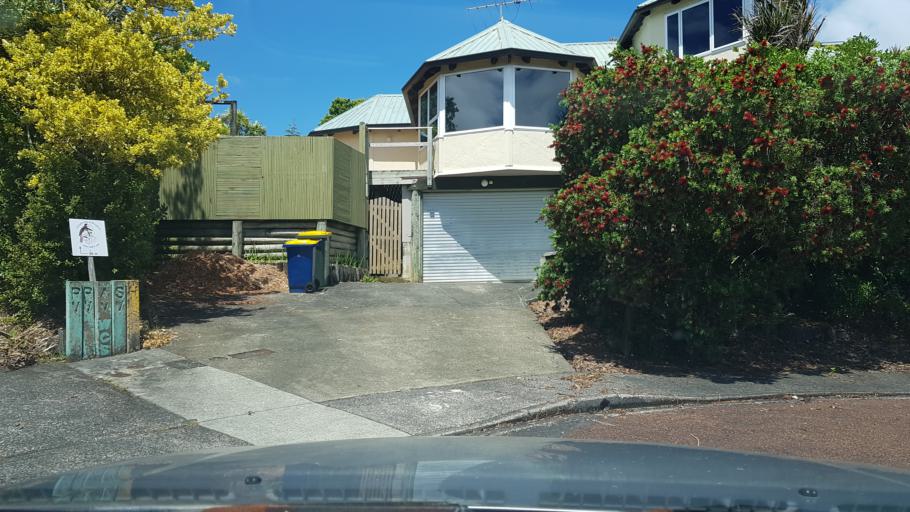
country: NZ
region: Auckland
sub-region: Auckland
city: North Shore
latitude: -36.8124
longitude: 174.7061
